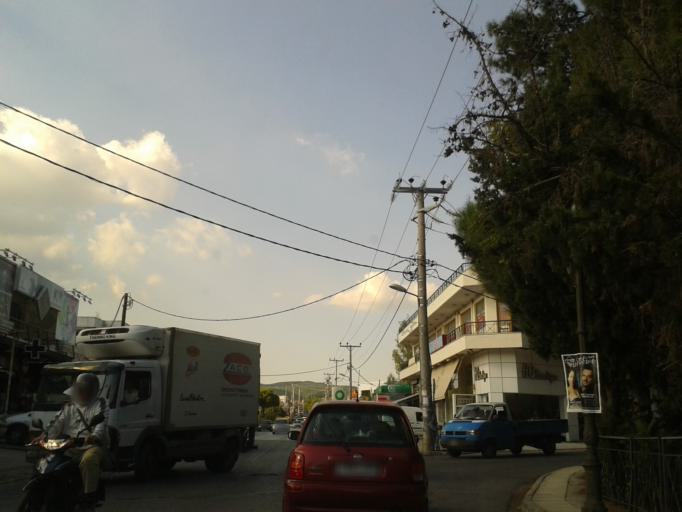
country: GR
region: Attica
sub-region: Nomarchia Anatolikis Attikis
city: Anoixi
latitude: 38.1362
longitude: 23.8567
